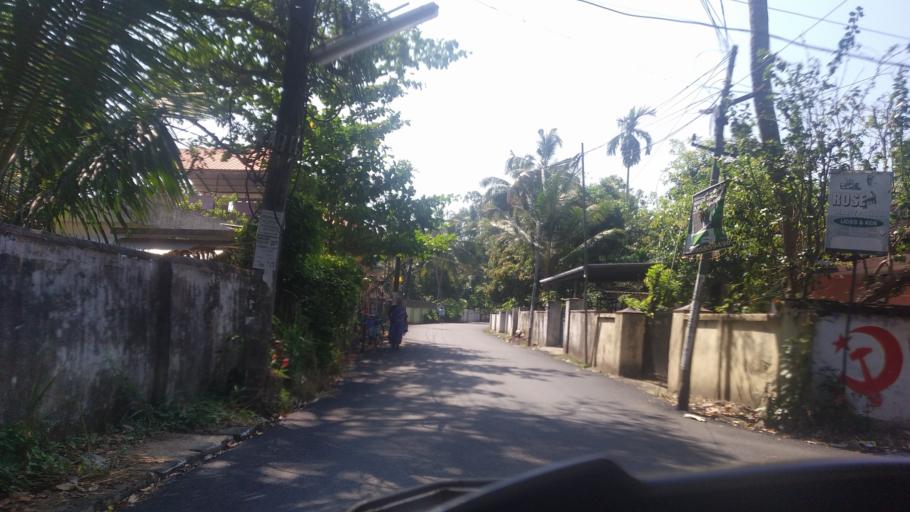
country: IN
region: Kerala
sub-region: Ernakulam
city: Elur
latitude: 10.0411
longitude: 76.2233
